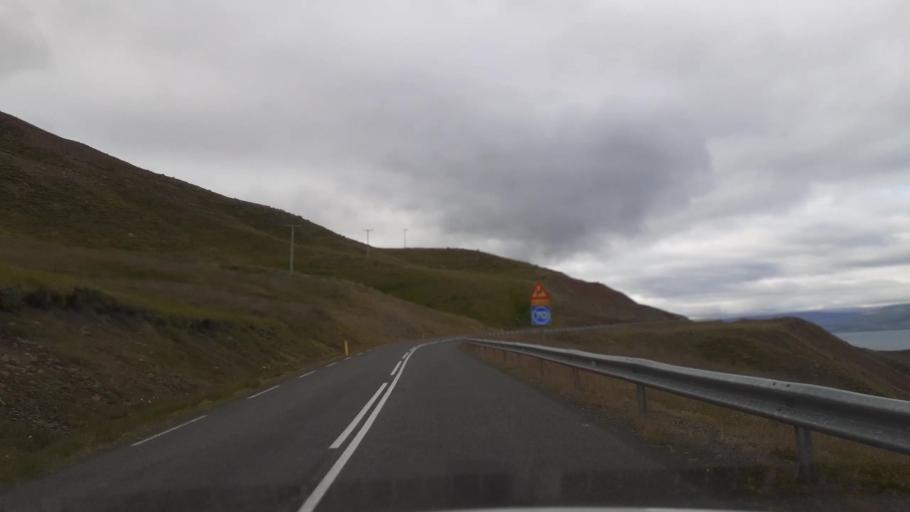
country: IS
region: Northeast
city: Akureyri
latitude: 65.8372
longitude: -18.0553
